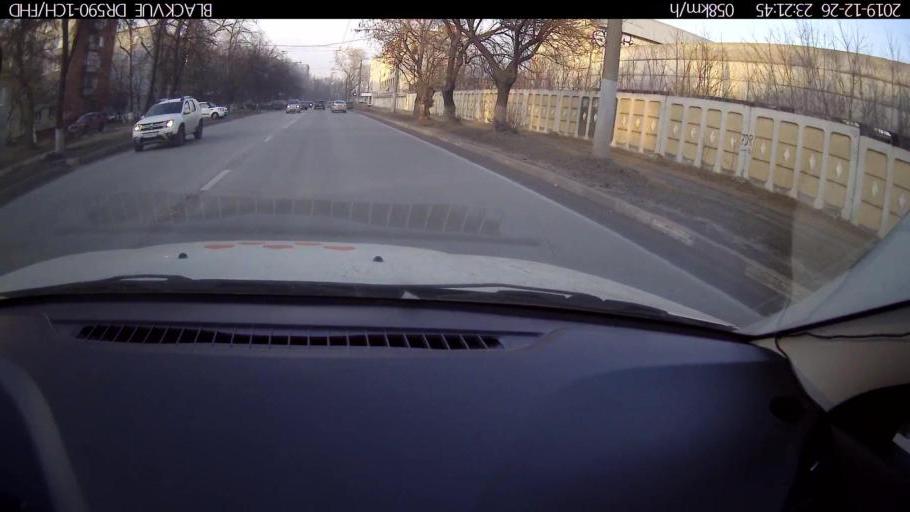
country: RU
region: Nizjnij Novgorod
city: Burevestnik
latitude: 56.2366
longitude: 43.8731
